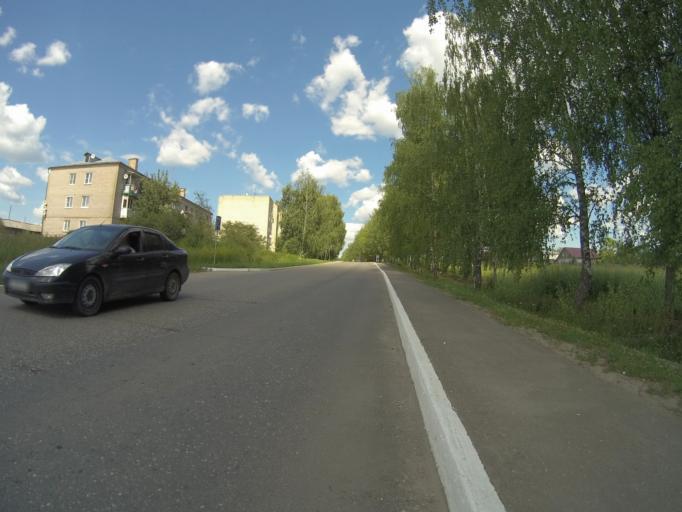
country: RU
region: Ivanovo
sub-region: Privolzhskiy Rayon
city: Ples
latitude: 57.4509
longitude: 41.5023
